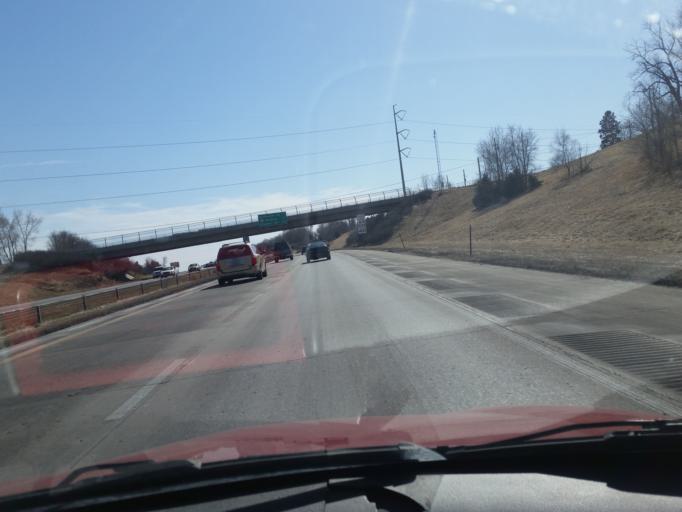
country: US
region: Nebraska
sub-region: Sarpy County
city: Offutt Air Force Base
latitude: 41.1778
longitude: -95.9396
